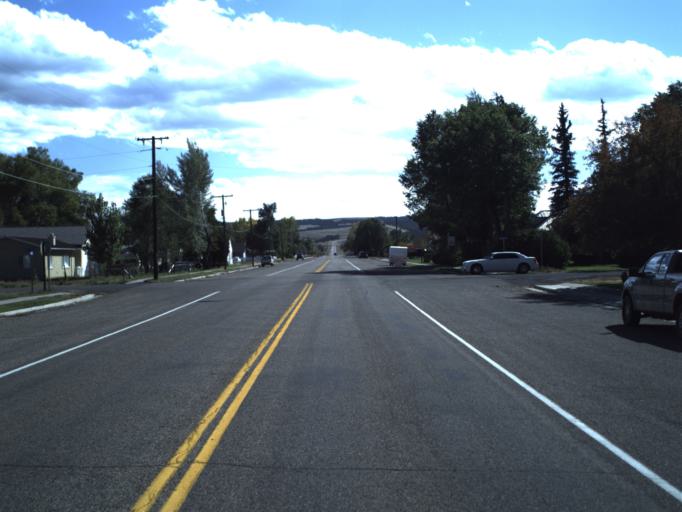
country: US
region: Utah
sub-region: Garfield County
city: Panguitch
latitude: 37.8202
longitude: -112.4356
